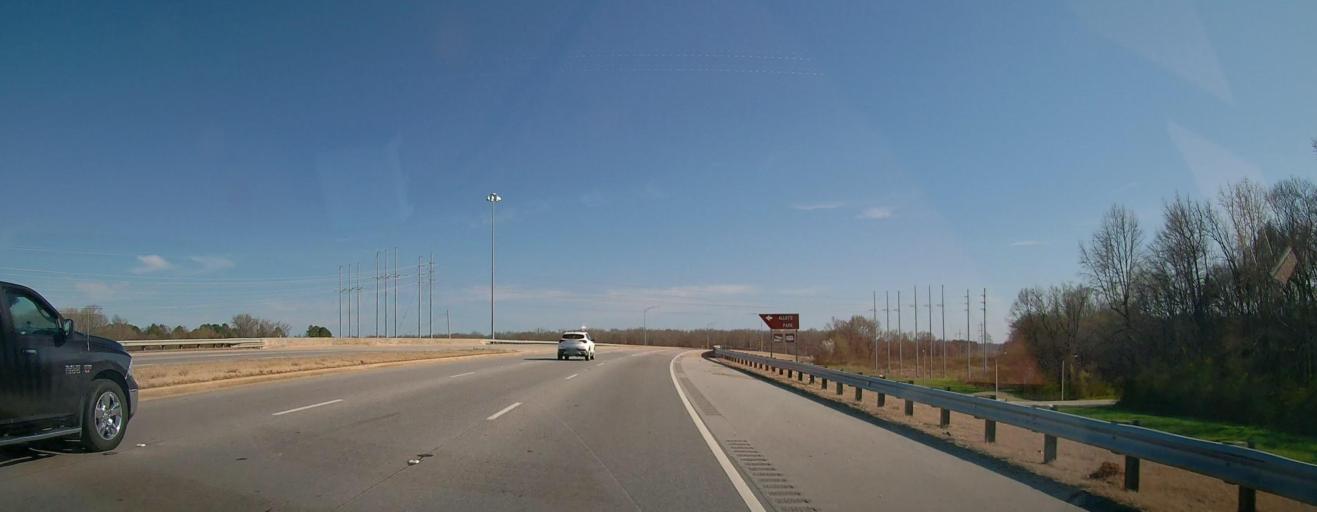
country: US
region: Alabama
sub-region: Lauderdale County
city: East Florence
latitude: 34.7835
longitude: -87.6356
